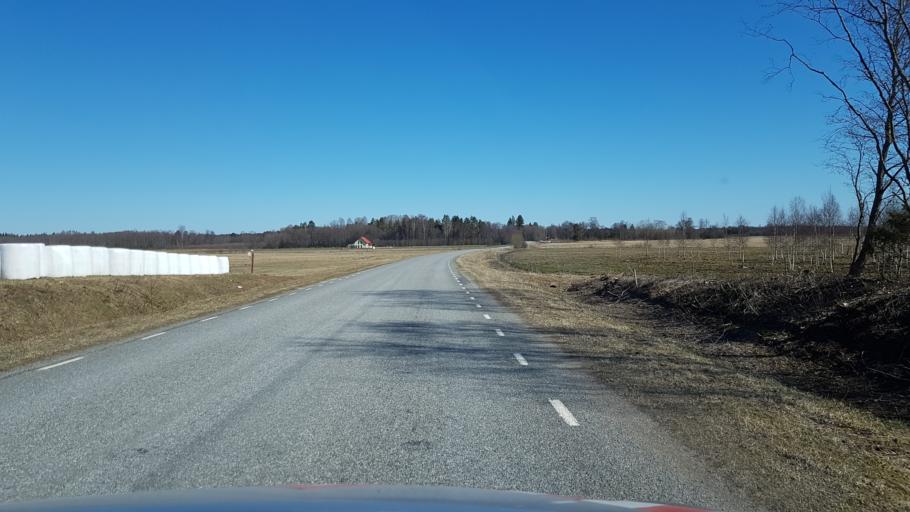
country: EE
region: Laeaene-Virumaa
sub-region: Haljala vald
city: Haljala
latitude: 59.4594
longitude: 26.2329
